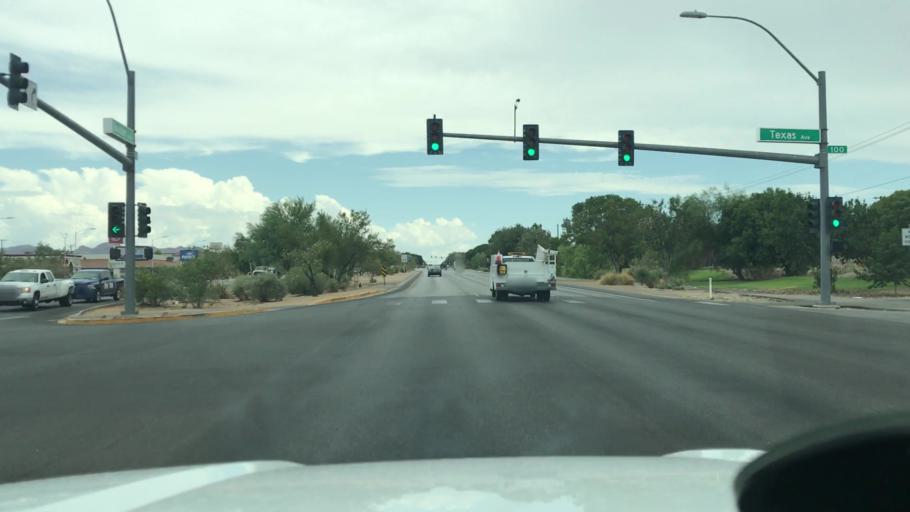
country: US
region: Nevada
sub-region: Clark County
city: Henderson
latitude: 36.0367
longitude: -114.9790
